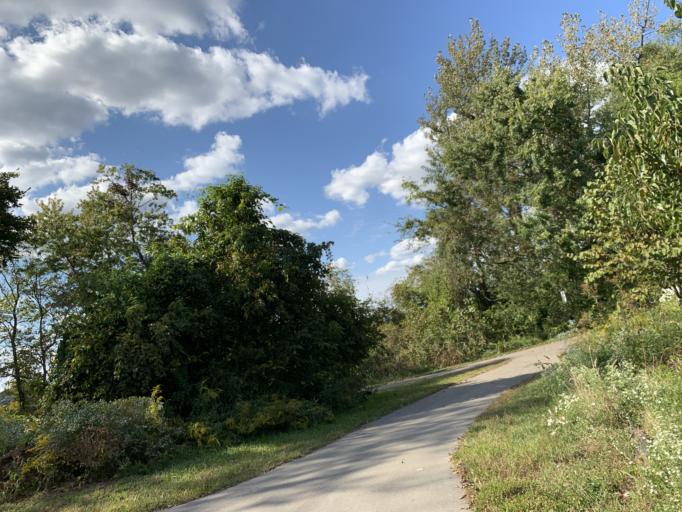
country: US
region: Indiana
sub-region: Floyd County
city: New Albany
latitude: 38.2660
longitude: -85.8293
